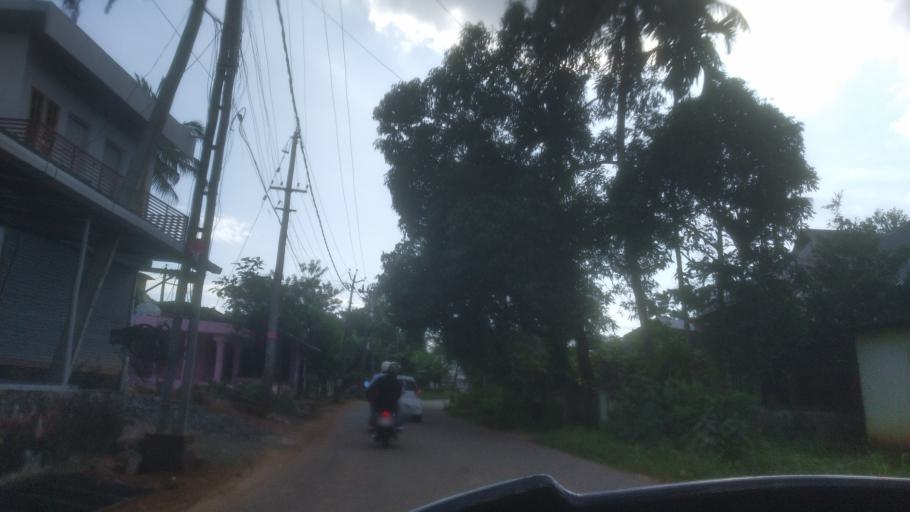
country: IN
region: Kerala
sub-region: Ernakulam
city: Muvattupula
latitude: 9.9957
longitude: 76.6062
